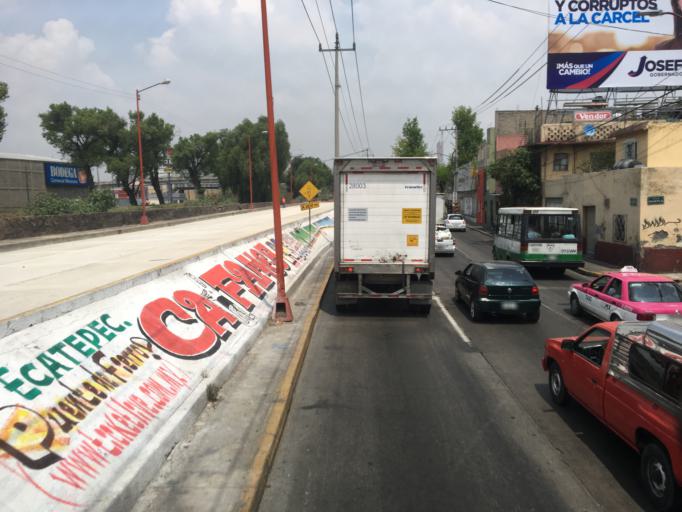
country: MX
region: Mexico
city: Tlalnepantla
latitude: 19.5294
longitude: -99.1675
